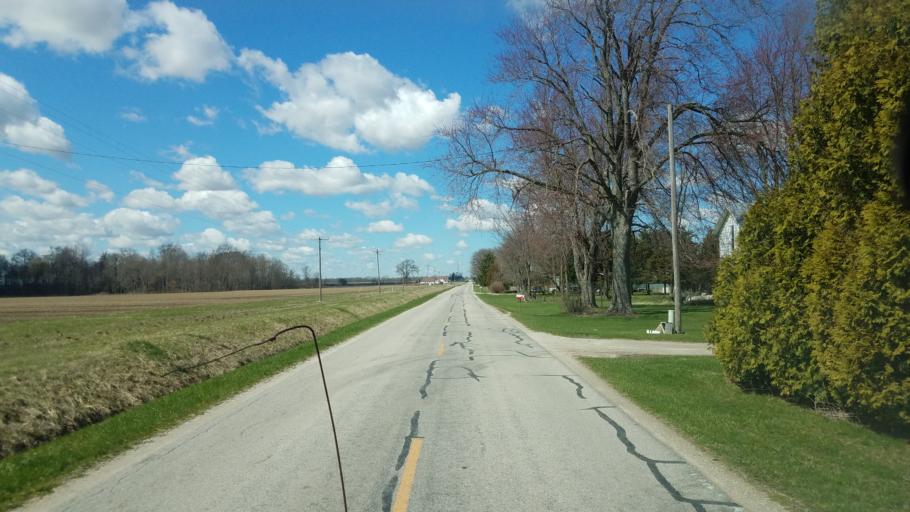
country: US
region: Ohio
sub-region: Sandusky County
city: Green Springs
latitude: 41.2421
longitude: -83.0331
